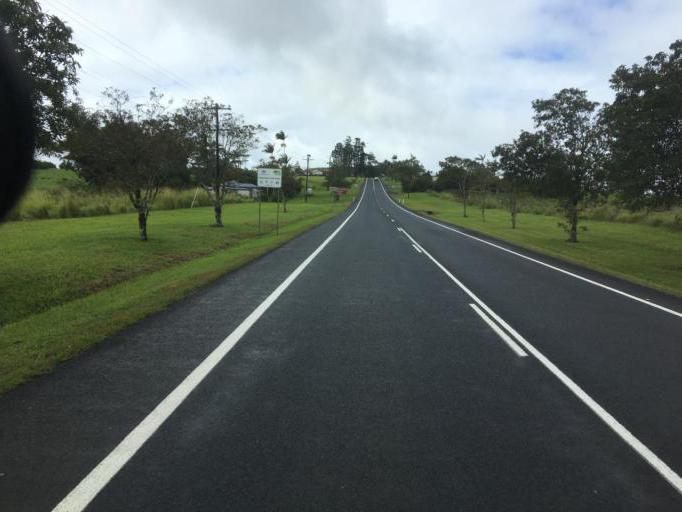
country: AU
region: Queensland
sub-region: Tablelands
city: Ravenshoe
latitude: -17.5089
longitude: 145.6180
